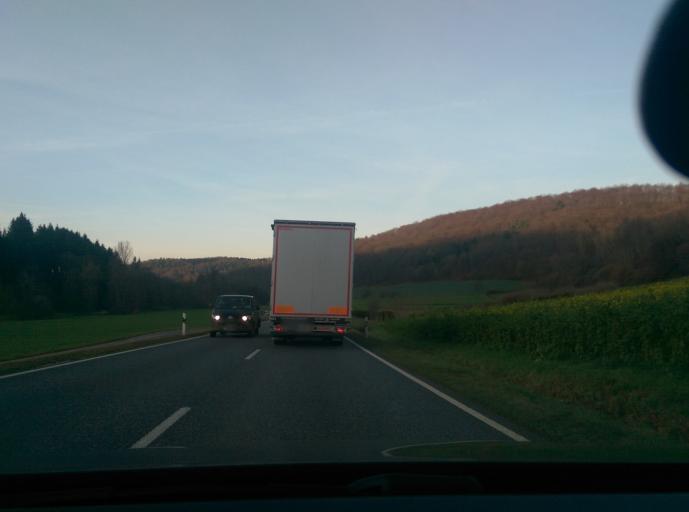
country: DE
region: Hesse
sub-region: Regierungsbezirk Kassel
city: Sontra
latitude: 51.0763
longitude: 9.9892
